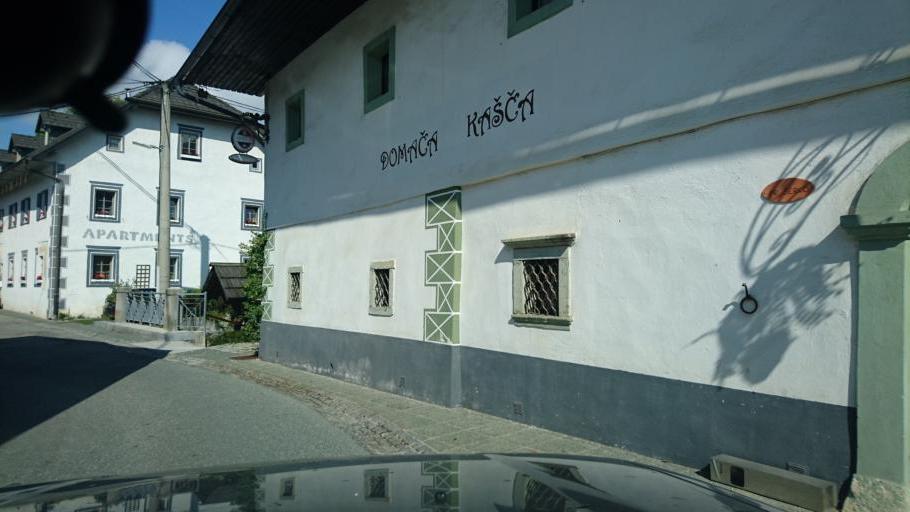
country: SI
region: Kranjska Gora
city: Kranjska Gora
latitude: 46.4938
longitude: 13.7570
